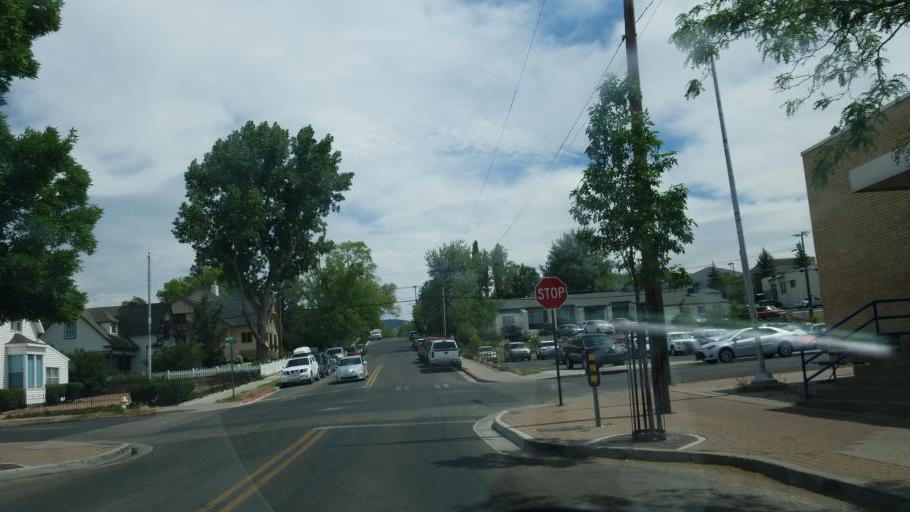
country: US
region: Arizona
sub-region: Coconino County
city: Flagstaff
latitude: 35.2000
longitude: -111.6479
